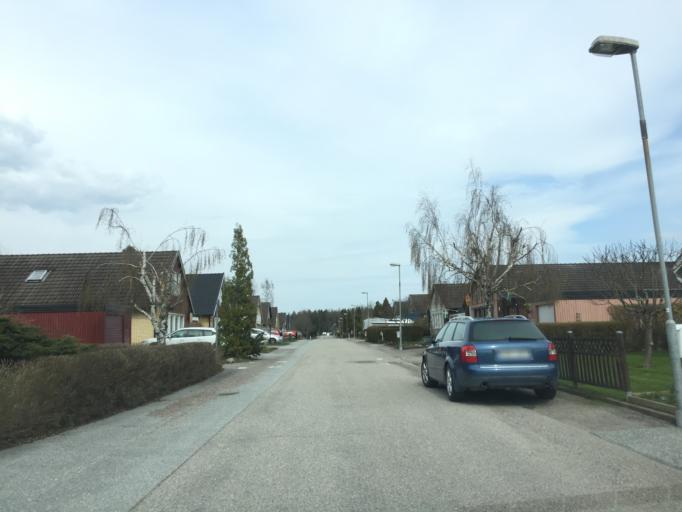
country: SE
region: OErebro
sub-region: Orebro Kommun
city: Orebro
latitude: 59.3114
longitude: 15.1774
